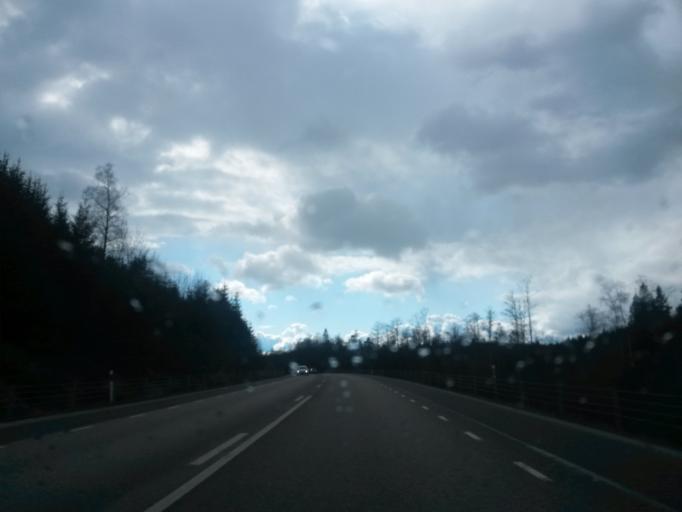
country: SE
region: Vaestra Goetaland
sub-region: Skovde Kommun
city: Skoevde
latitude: 58.3929
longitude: 13.7625
